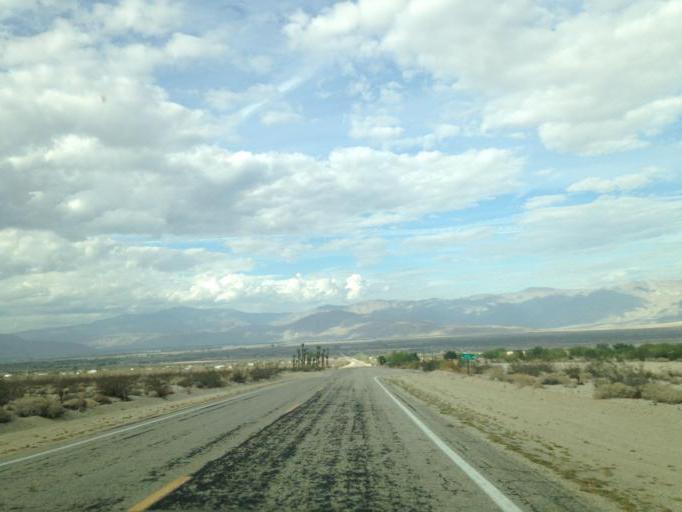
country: US
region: California
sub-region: San Diego County
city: Borrego Springs
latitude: 33.1921
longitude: -116.3305
